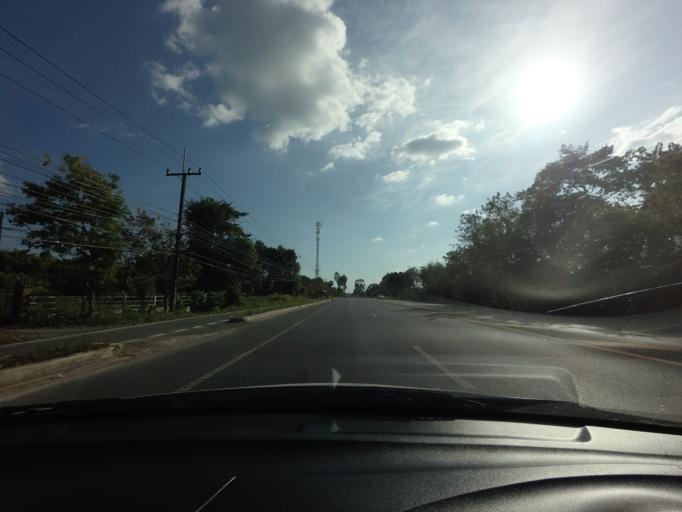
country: TH
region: Nakhon Nayok
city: Nakhon Nayok
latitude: 14.2819
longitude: 101.2759
